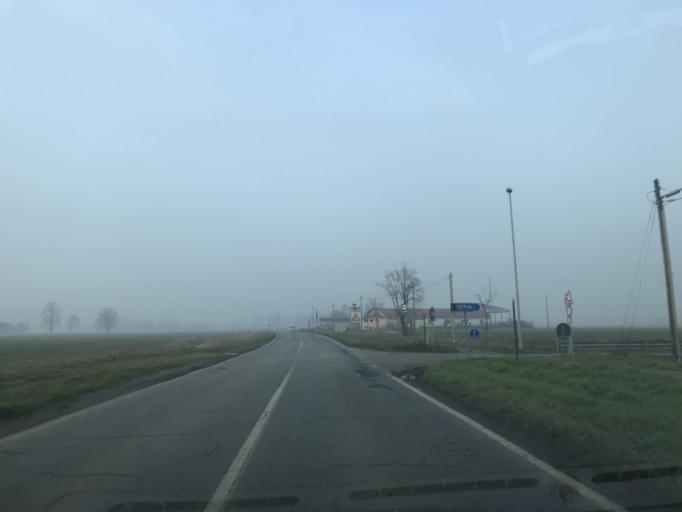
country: IT
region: Lombardy
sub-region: Provincia di Lodi
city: Ossago Lodigiano
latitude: 45.2524
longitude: 9.5360
